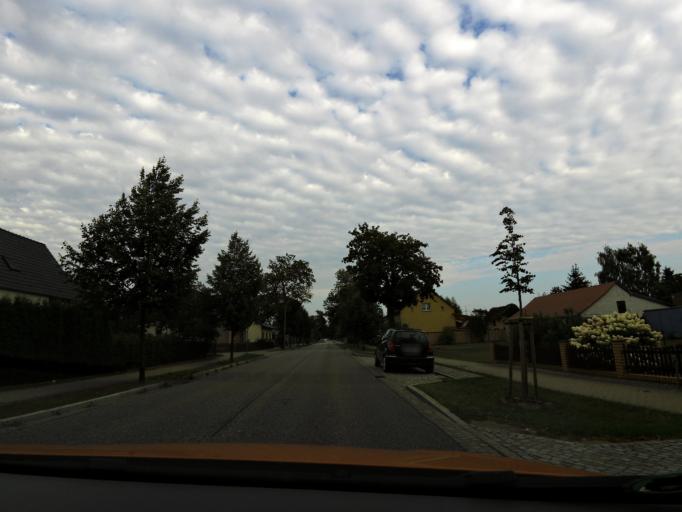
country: DE
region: Brandenburg
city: Gross Kreutz
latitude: 52.4016
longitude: 12.7918
